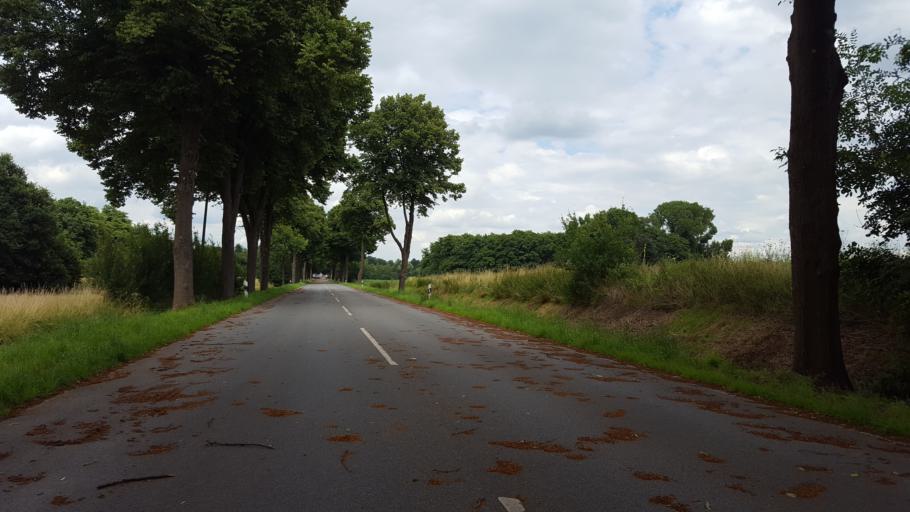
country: DE
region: North Rhine-Westphalia
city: Oer-Erkenschwick
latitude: 51.6405
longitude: 7.2895
